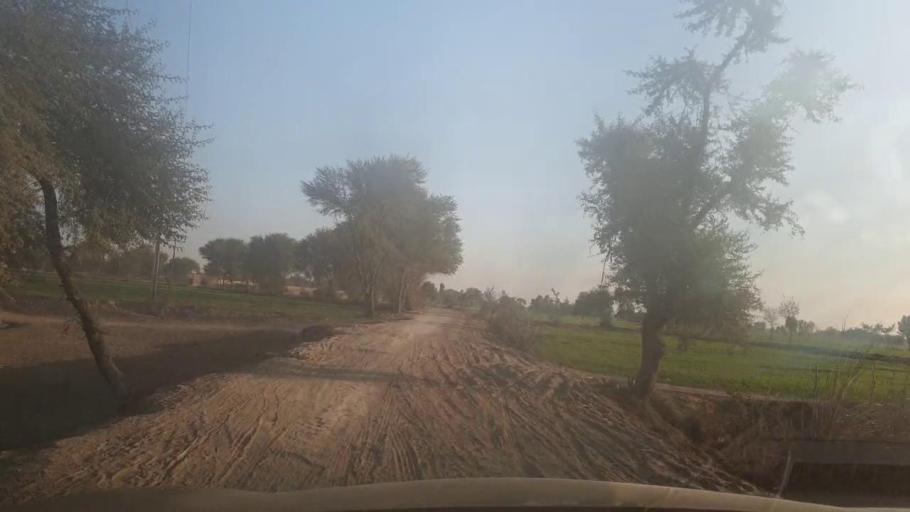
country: PK
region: Sindh
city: Mirpur Mathelo
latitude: 28.1708
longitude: 69.5778
